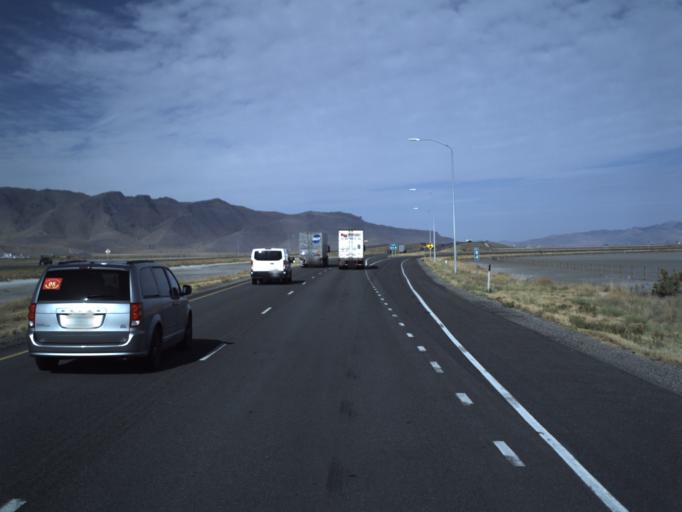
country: US
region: Utah
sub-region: Tooele County
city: Grantsville
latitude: 40.7063
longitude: -112.5178
